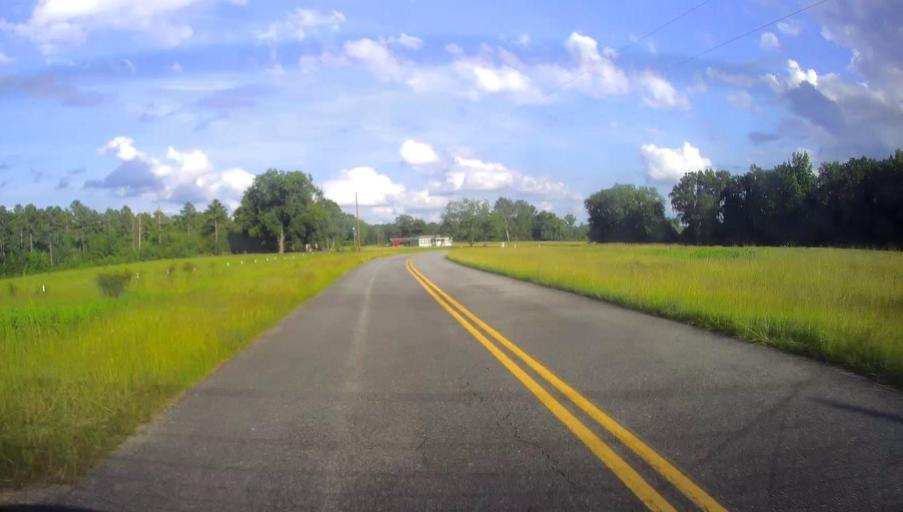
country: US
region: Georgia
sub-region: Crawford County
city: Roberta
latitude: 32.7340
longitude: -84.0080
